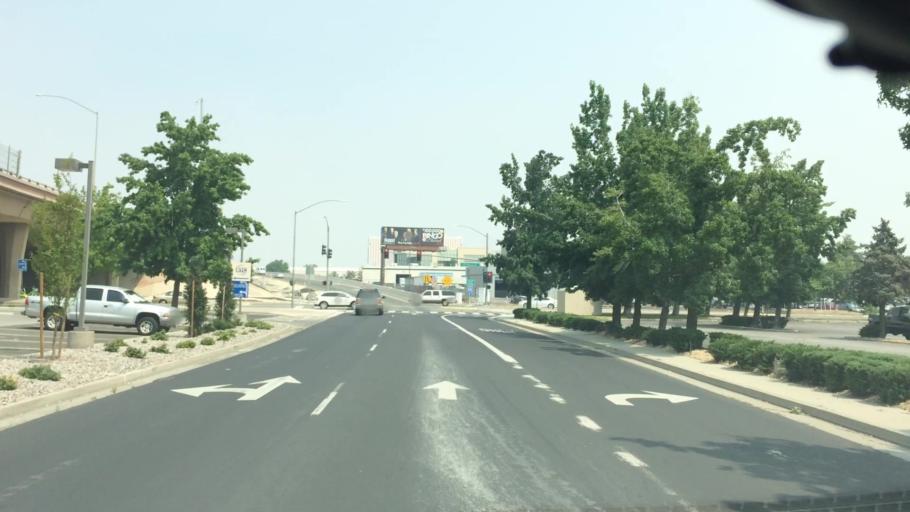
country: US
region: Nevada
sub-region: Washoe County
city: Sparks
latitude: 39.5086
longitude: -119.7797
